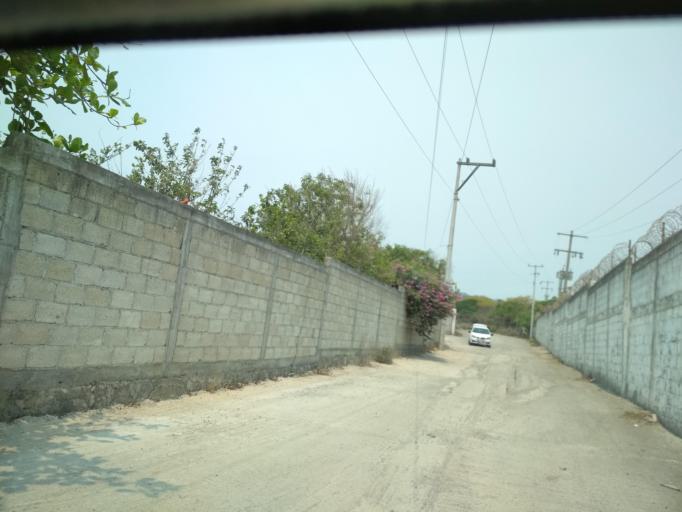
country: MX
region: Veracruz
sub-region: Veracruz
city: Delfino Victoria (Santa Fe)
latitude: 19.2257
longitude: -96.2602
